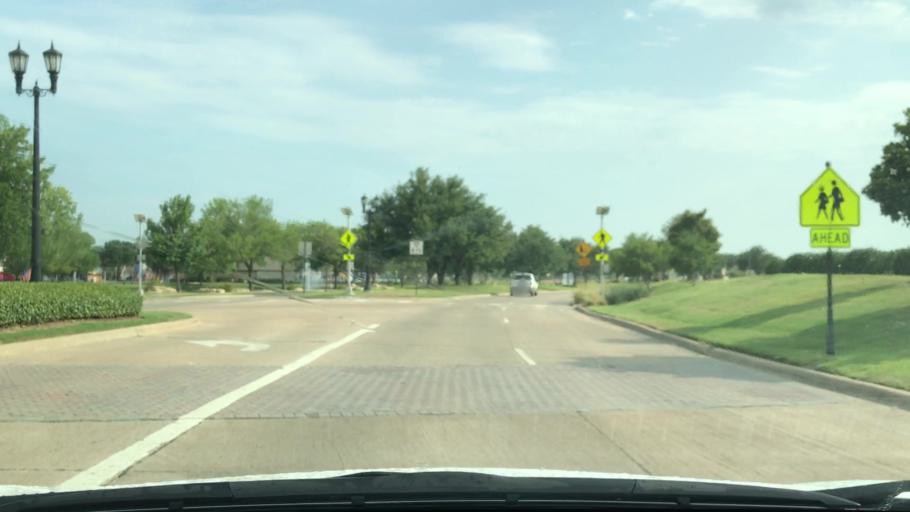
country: US
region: Texas
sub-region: Dallas County
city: Rowlett
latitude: 32.9391
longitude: -96.5333
